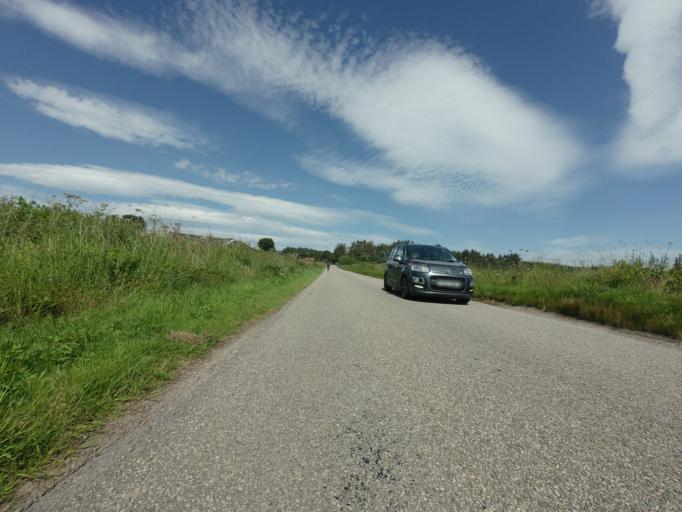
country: GB
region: Scotland
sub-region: Highland
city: Inverness
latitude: 57.5291
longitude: -4.3196
